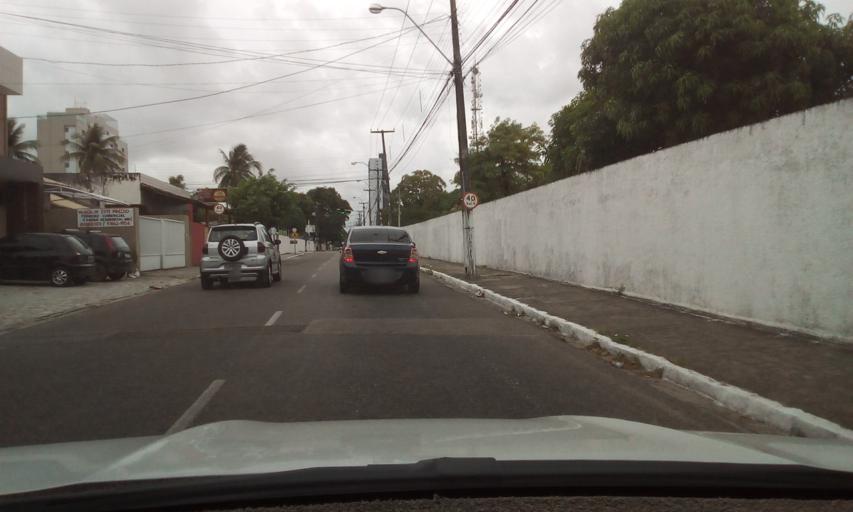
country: BR
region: Paraiba
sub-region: Joao Pessoa
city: Joao Pessoa
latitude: -7.1151
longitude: -34.8611
